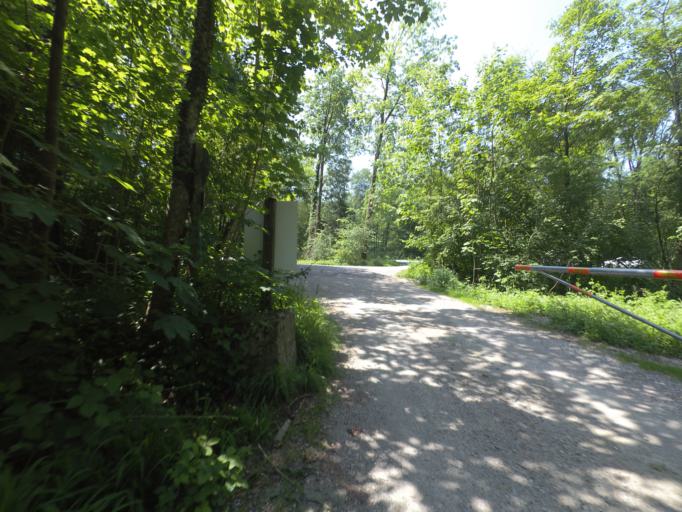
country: AT
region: Salzburg
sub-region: Politischer Bezirk Salzburg-Umgebung
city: Anif
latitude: 47.7558
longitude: 13.0748
